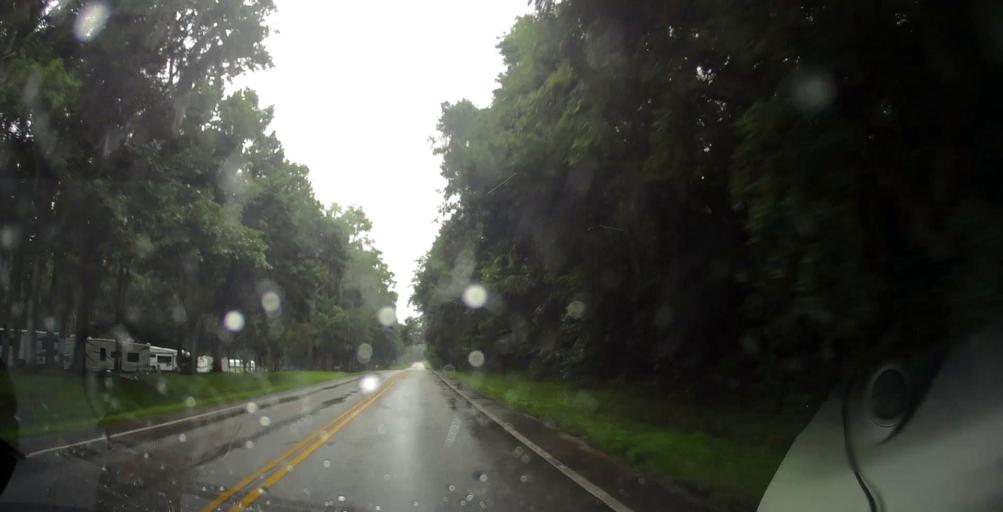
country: US
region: Florida
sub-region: Marion County
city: Citra
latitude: 29.3957
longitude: -82.2474
